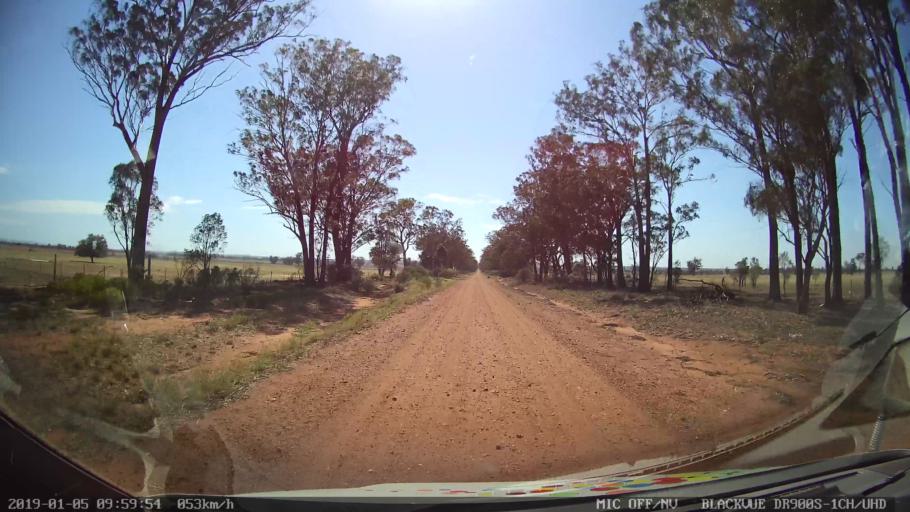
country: AU
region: New South Wales
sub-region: Gilgandra
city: Gilgandra
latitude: -31.6680
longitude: 148.8219
